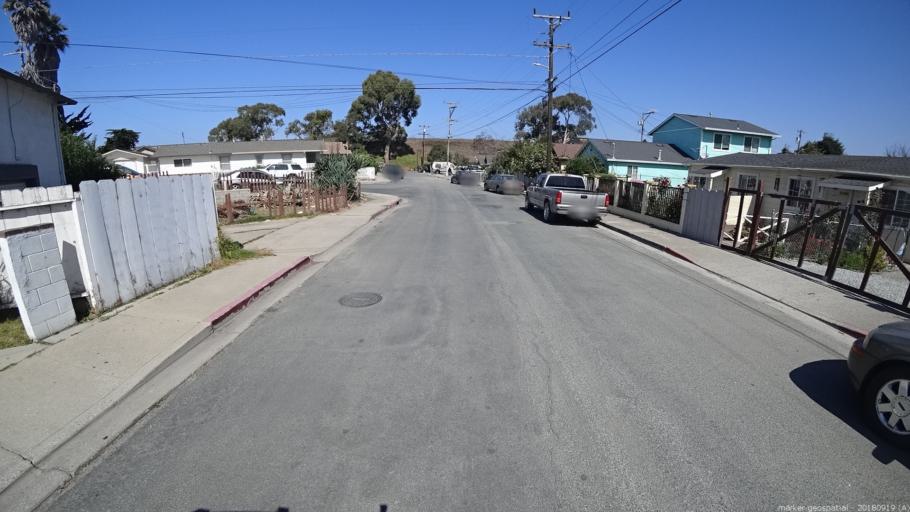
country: US
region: California
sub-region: Monterey County
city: Castroville
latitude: 36.7650
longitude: -121.7474
